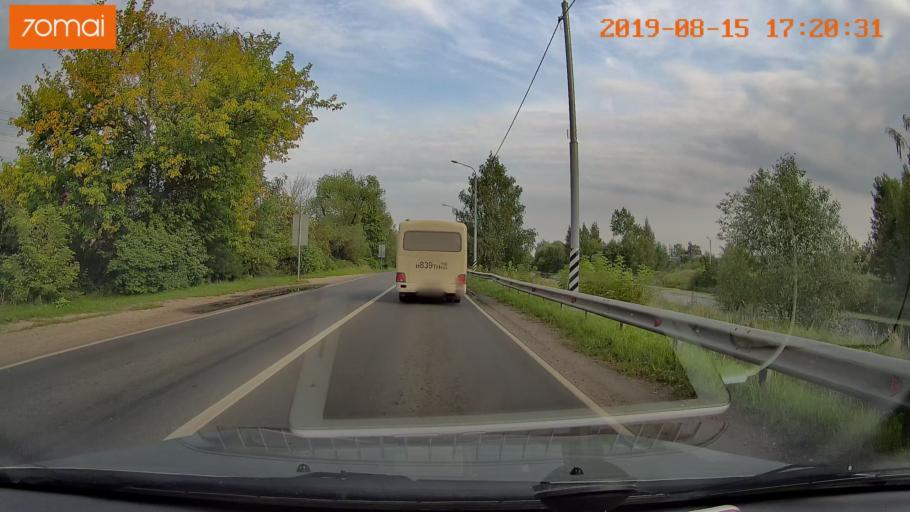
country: RU
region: Moskovskaya
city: Ashitkovo
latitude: 55.4244
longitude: 38.5587
